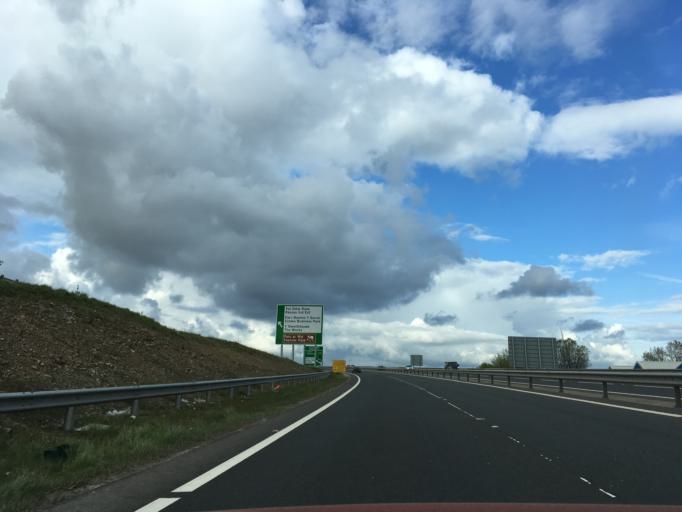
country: GB
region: Wales
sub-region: Blaenau Gwent
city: Tredegar
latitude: 51.7905
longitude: -3.2508
